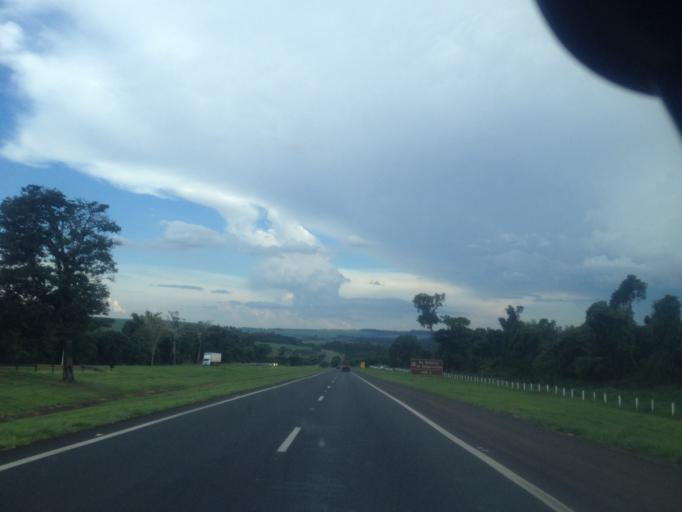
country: BR
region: Sao Paulo
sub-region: Santa Rita Do Passa Quatro
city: Santa Rita do Passa Quatro
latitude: -21.7210
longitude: -47.5888
